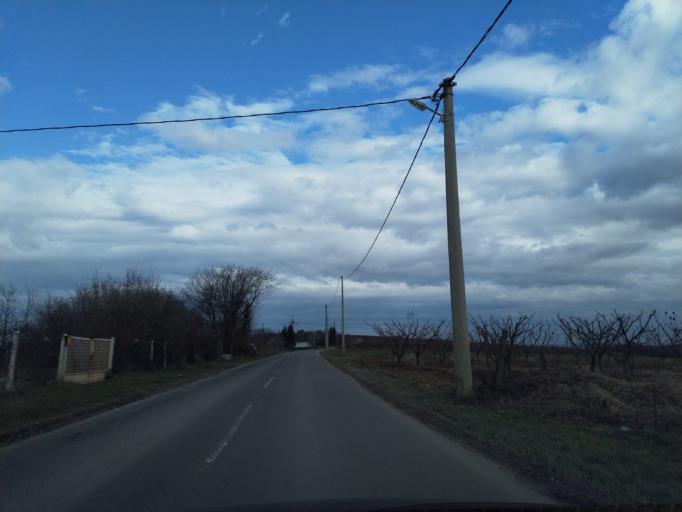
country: RS
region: Central Serbia
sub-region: Belgrade
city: Grocka
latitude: 44.6276
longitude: 20.7446
